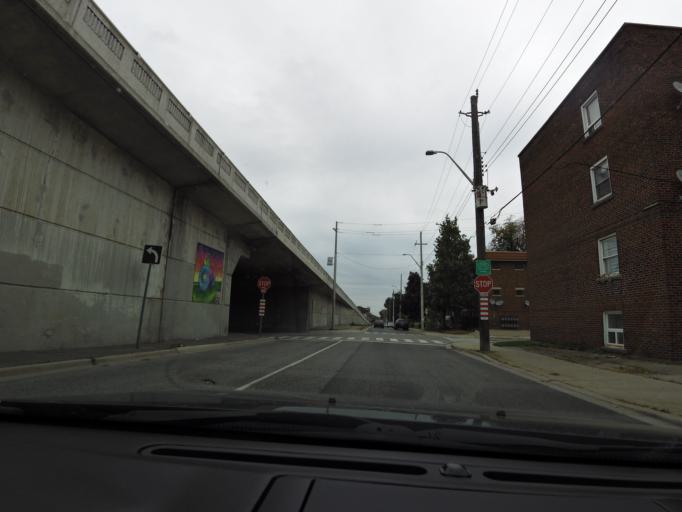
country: CA
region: Ontario
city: Hamilton
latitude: 43.2488
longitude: -79.8586
